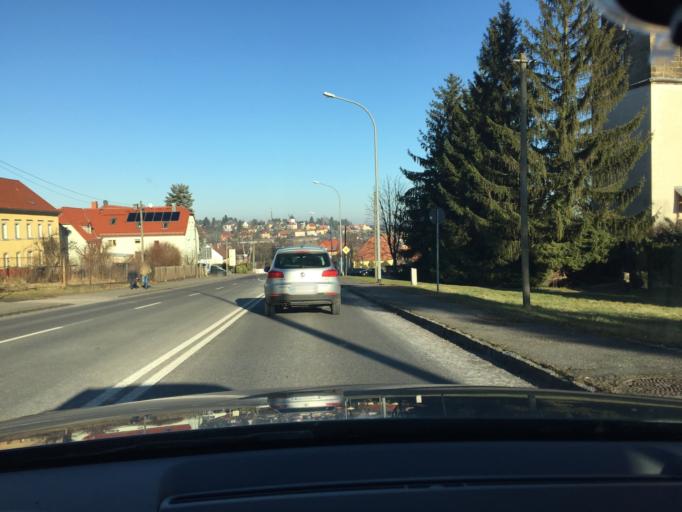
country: DE
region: Saxony
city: Bannewitz
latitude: 50.9643
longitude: 13.7108
